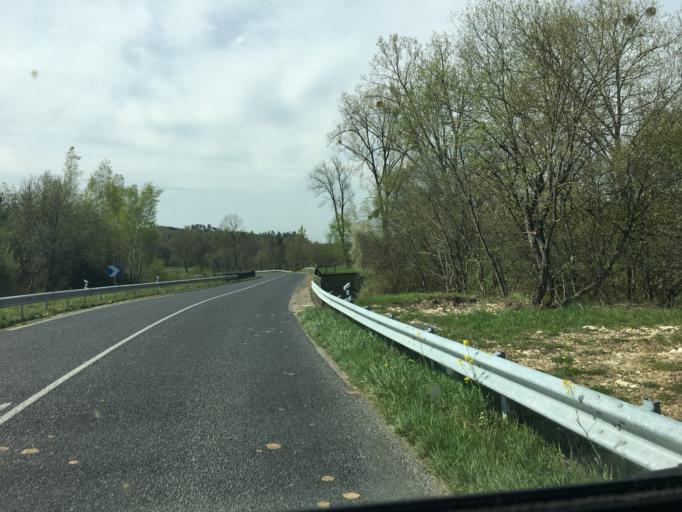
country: FR
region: Lorraine
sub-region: Departement de la Meuse
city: Saint-Mihiel
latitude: 48.8487
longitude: 5.5135
